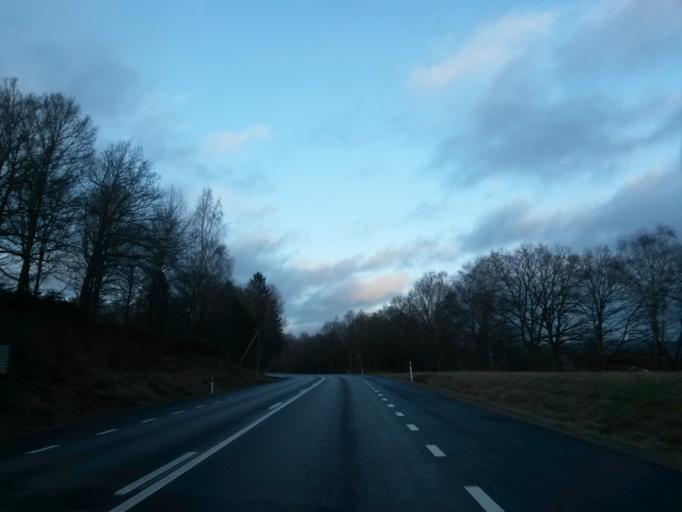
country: SE
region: Halland
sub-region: Halmstads Kommun
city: Aled
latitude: 56.7511
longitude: 12.9402
